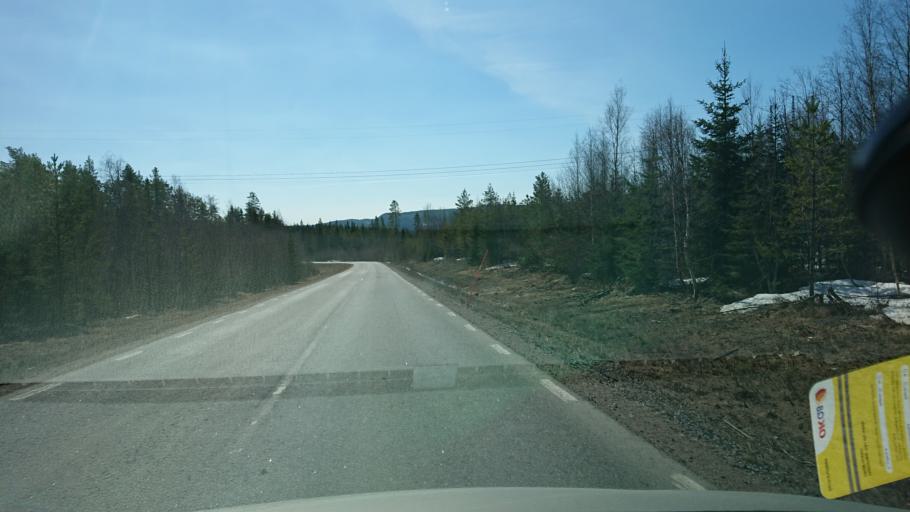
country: SE
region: Vaesternorrland
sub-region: Solleftea Kommun
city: As
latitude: 63.5816
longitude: 16.4359
